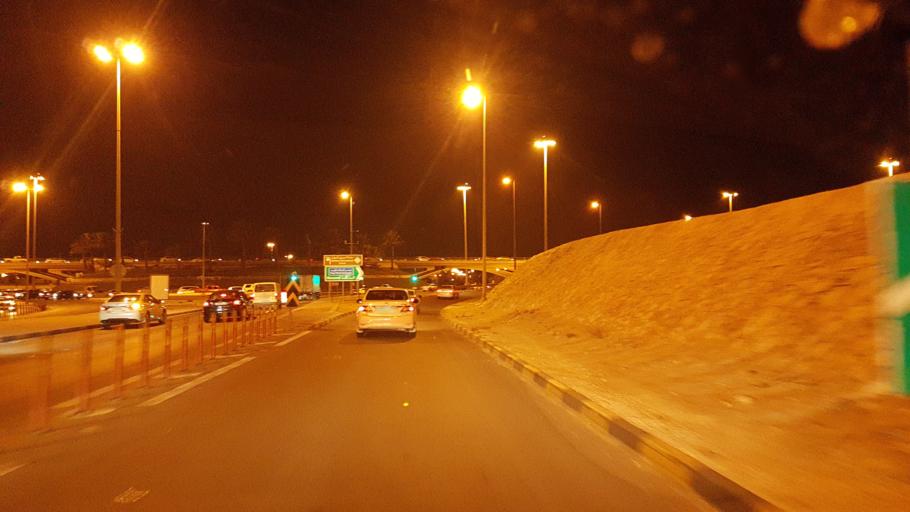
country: BH
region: Central Governorate
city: Madinat Hamad
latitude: 26.1397
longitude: 50.5126
